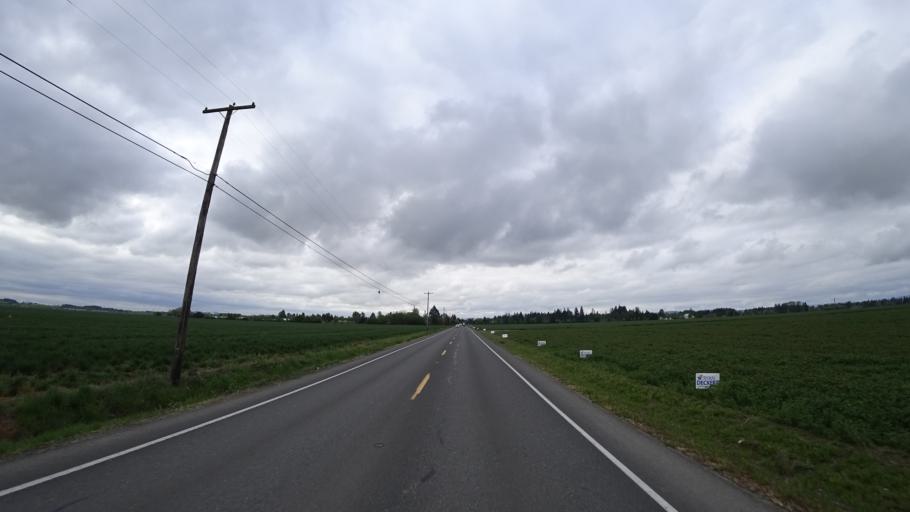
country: US
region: Oregon
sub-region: Washington County
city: Hillsboro
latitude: 45.5569
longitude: -122.9731
